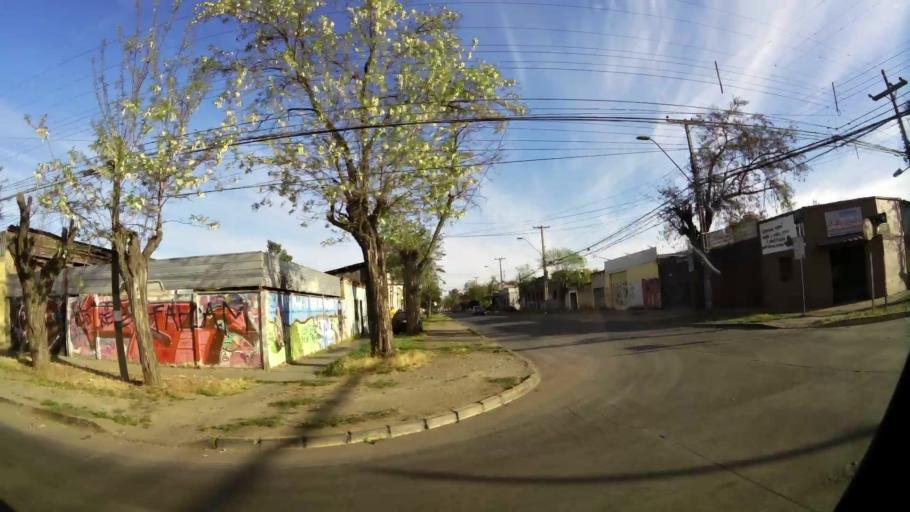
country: CL
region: Santiago Metropolitan
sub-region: Provincia de Santiago
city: Lo Prado
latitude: -33.4359
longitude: -70.6984
